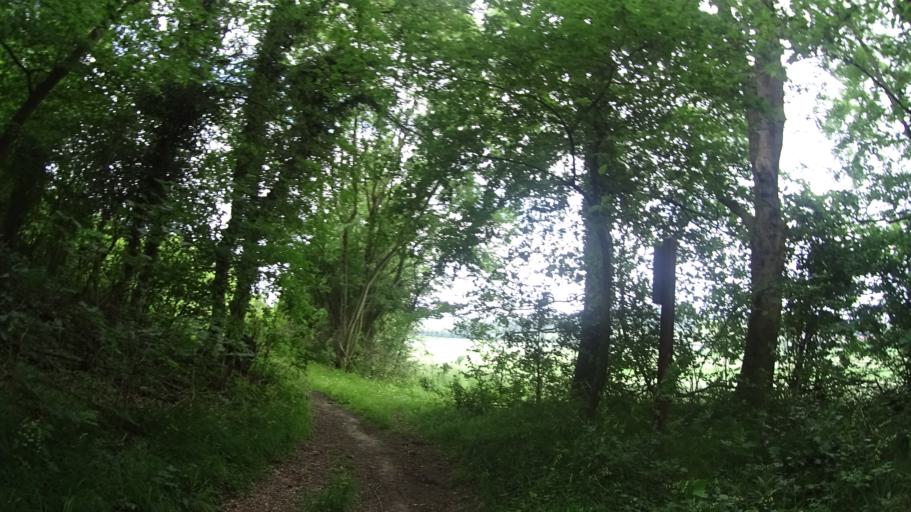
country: DE
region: Lower Saxony
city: Giesen
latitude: 52.1517
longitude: 9.8996
